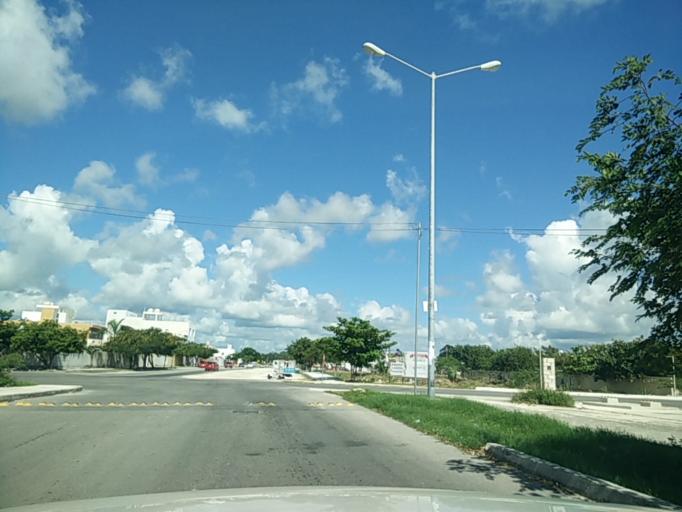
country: MX
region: Quintana Roo
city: Playa del Carmen
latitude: 20.6639
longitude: -87.0645
